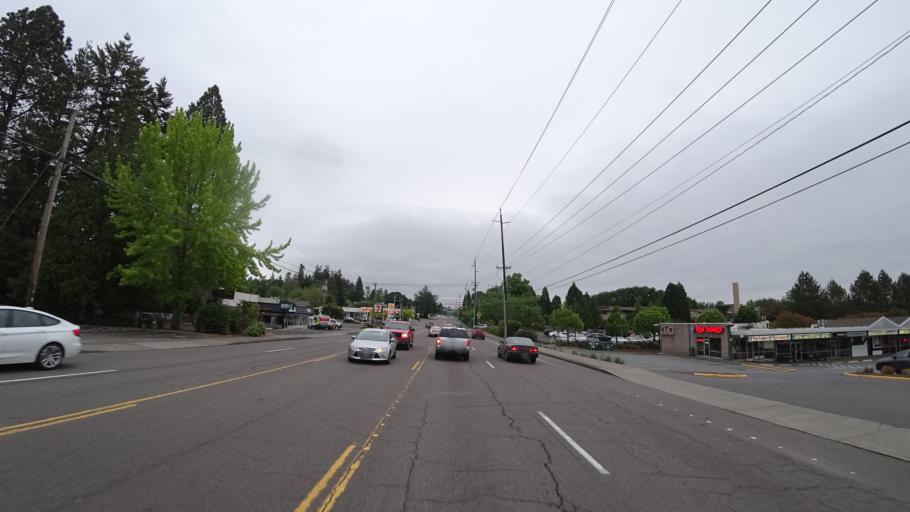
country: US
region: Oregon
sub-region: Washington County
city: Raleigh Hills
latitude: 45.4864
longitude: -122.7725
